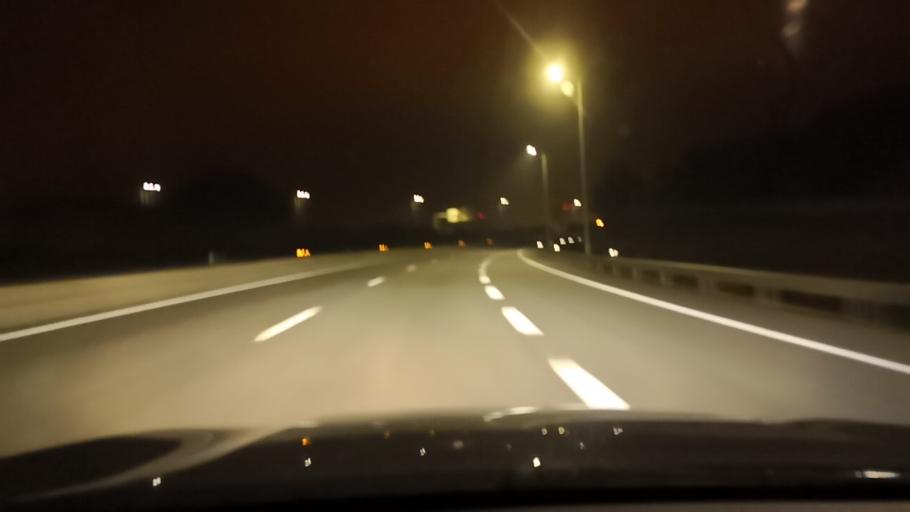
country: PT
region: Setubal
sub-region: Palmela
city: Palmela
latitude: 38.5802
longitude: -8.8631
